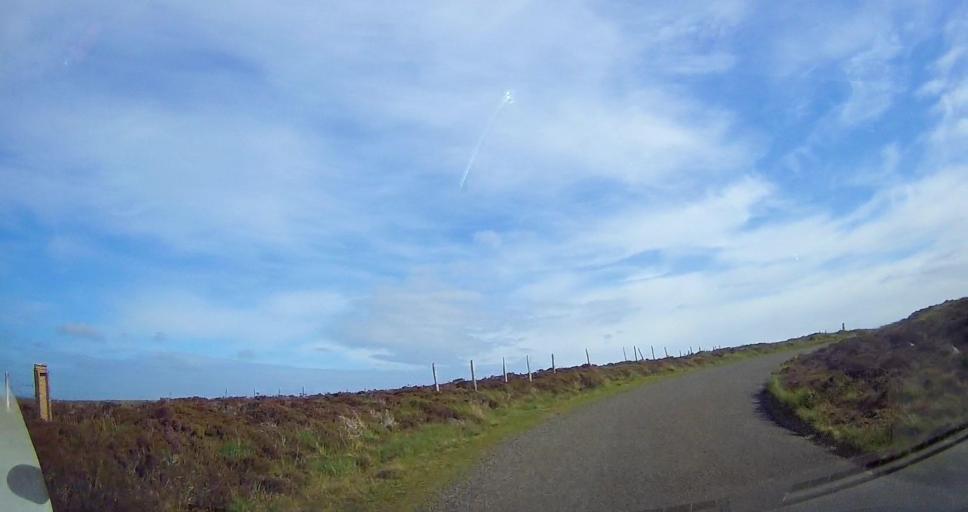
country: GB
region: Scotland
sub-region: Orkney Islands
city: Stromness
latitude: 58.8665
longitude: -3.2198
